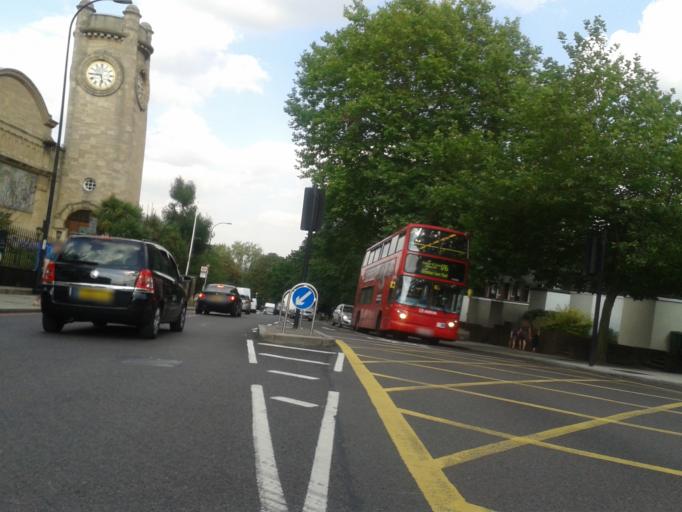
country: GB
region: England
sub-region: Greater London
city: Catford
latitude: 51.4406
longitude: -0.0616
